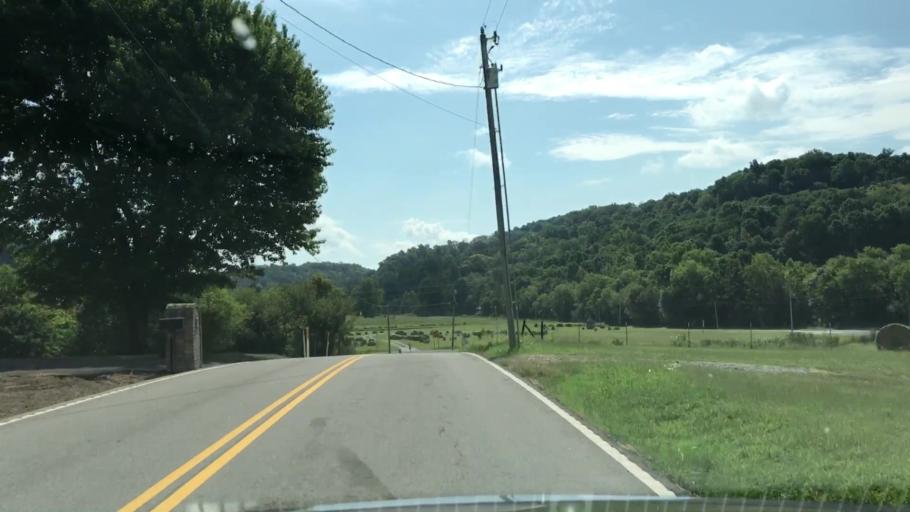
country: US
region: Tennessee
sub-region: Trousdale County
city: Hartsville
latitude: 36.4662
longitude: -86.1745
